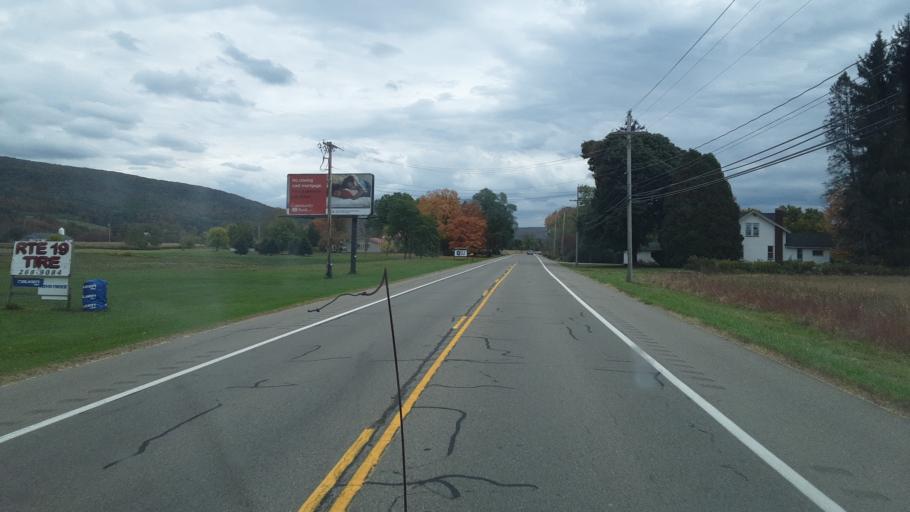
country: US
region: New York
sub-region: Allegany County
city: Belmont
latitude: 42.2037
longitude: -78.0068
